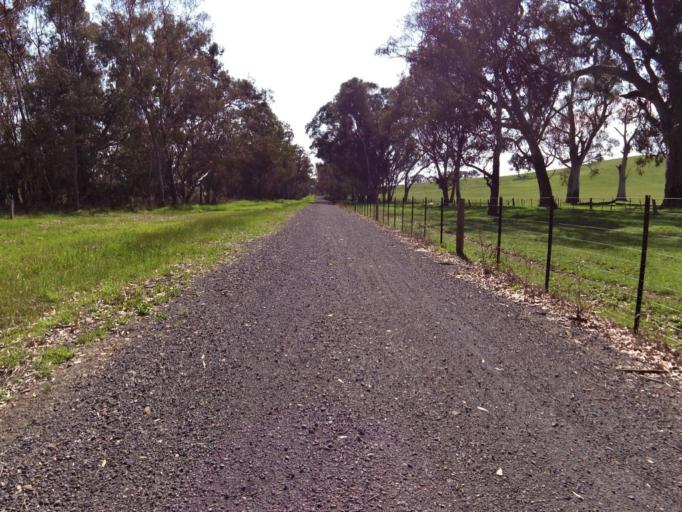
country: AU
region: Victoria
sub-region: Murrindindi
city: Alexandra
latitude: -37.1408
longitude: 145.5898
